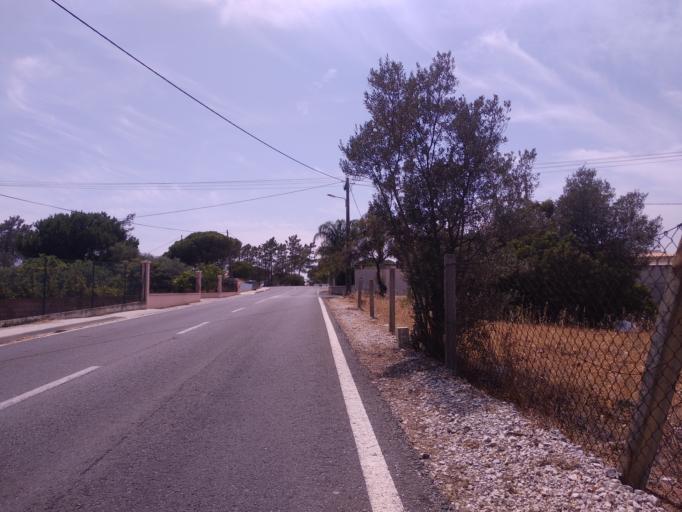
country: PT
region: Faro
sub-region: Faro
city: Santa Barbara de Nexe
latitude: 37.0861
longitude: -7.9921
